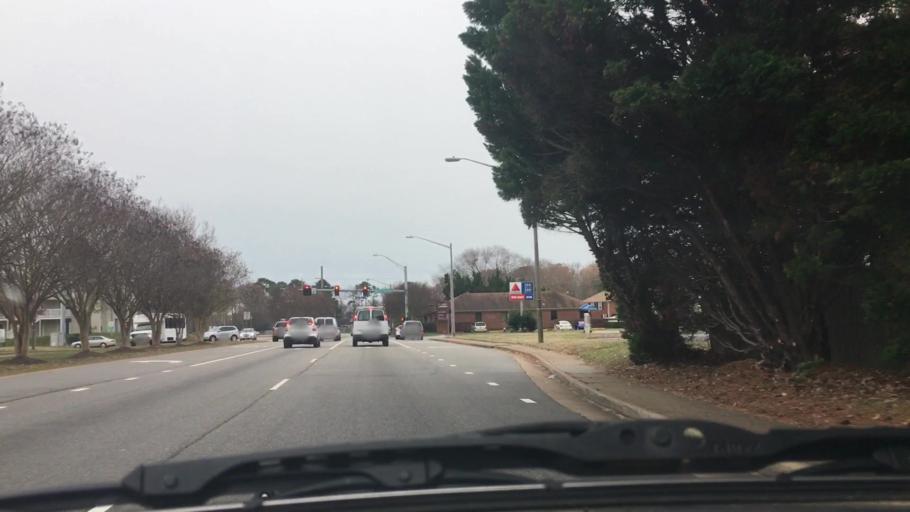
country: US
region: Virginia
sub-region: City of Chesapeake
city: Chesapeake
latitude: 36.8178
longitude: -76.1271
